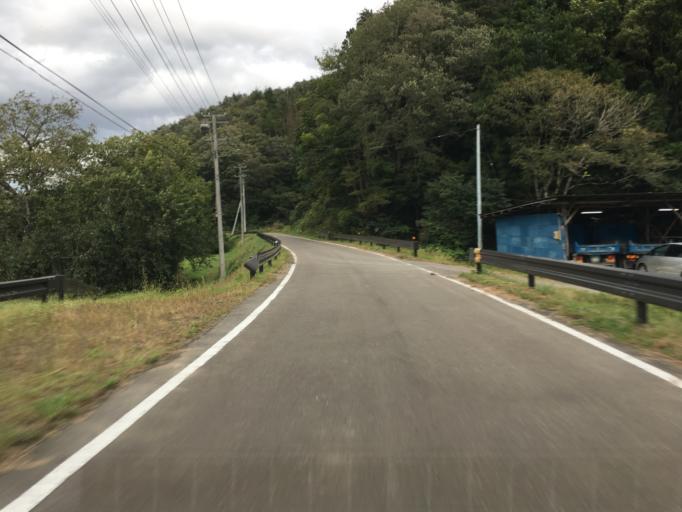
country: JP
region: Miyagi
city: Marumori
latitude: 37.9239
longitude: 140.7516
